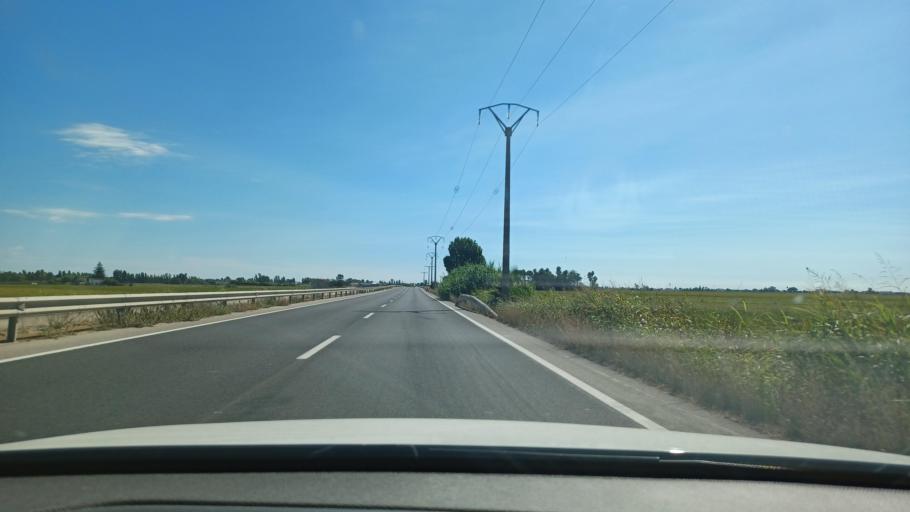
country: ES
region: Catalonia
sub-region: Provincia de Tarragona
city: Deltebre
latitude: 40.7108
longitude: 0.6707
